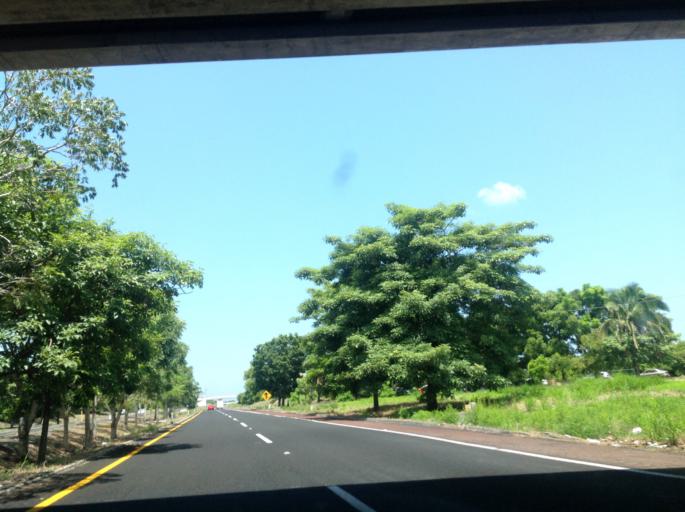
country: MX
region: Veracruz
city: El Tejar
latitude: 19.0832
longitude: -96.1974
